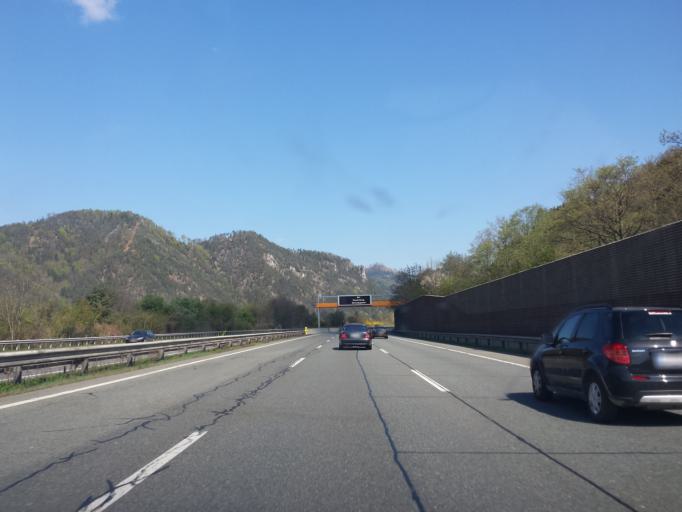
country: AT
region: Styria
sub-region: Politischer Bezirk Graz-Umgebung
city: Gratkorn
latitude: 47.1531
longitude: 15.3265
